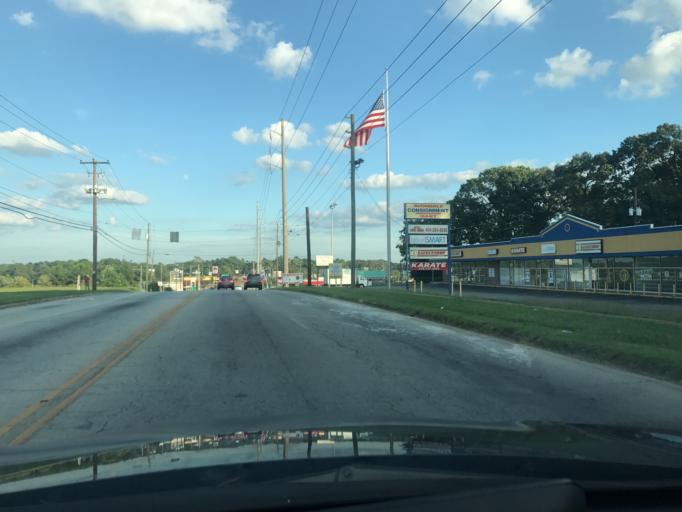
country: US
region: Georgia
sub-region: DeKalb County
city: Belvedere Park
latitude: 33.7566
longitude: -84.2708
